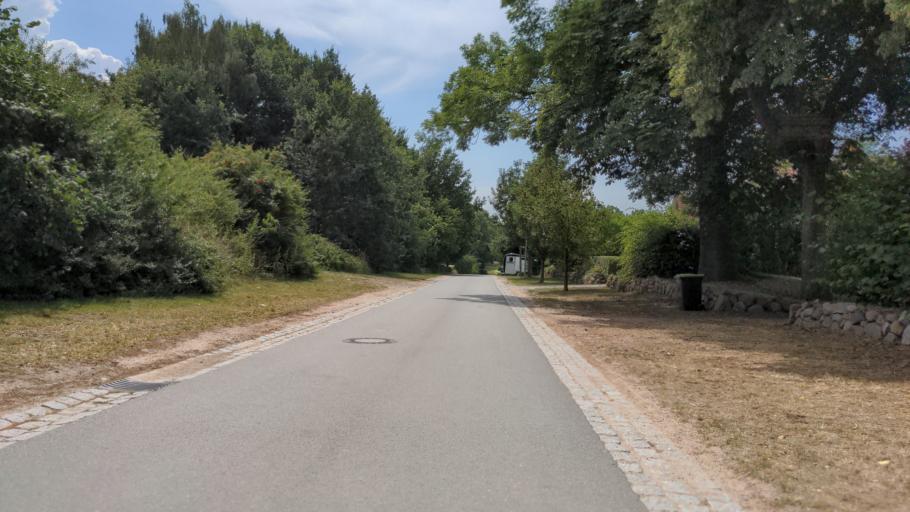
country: DE
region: Mecklenburg-Vorpommern
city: Selmsdorf
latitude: 53.8531
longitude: 10.7963
